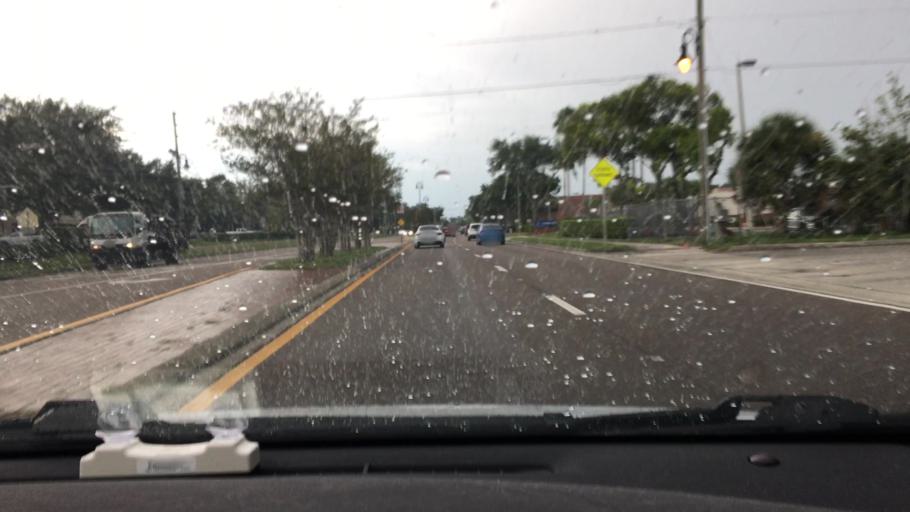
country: US
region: Florida
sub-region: Seminole County
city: Longwood
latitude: 28.6858
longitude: -81.3459
